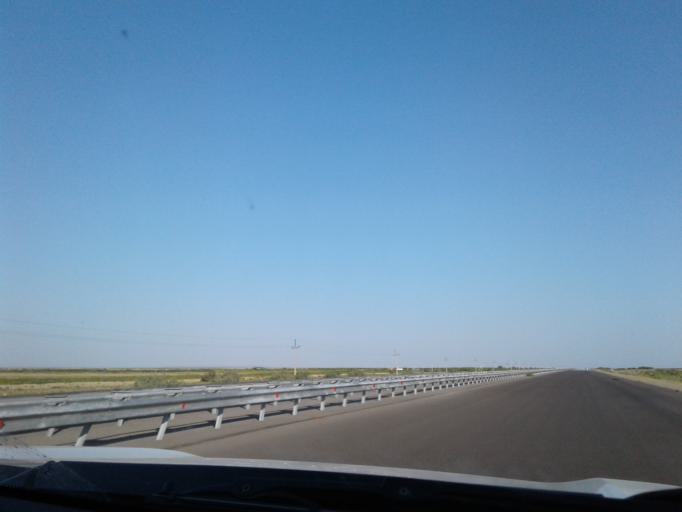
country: TM
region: Balkan
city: Serdar
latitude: 38.8826
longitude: 56.5483
